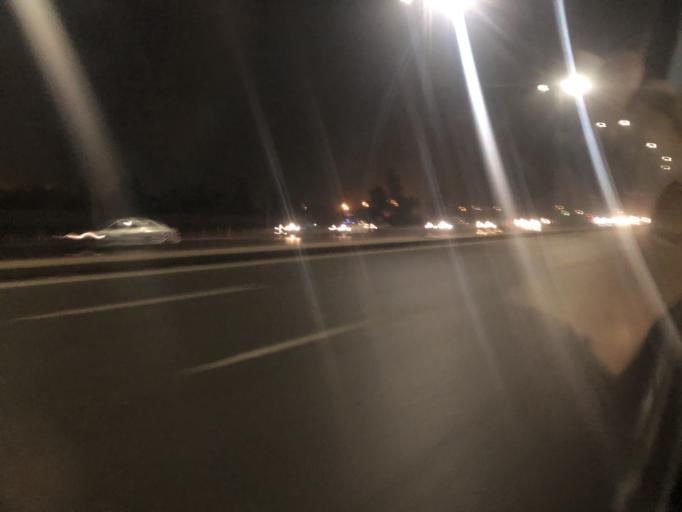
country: EG
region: Al Jizah
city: Al Jizah
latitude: 29.9845
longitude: 31.1242
